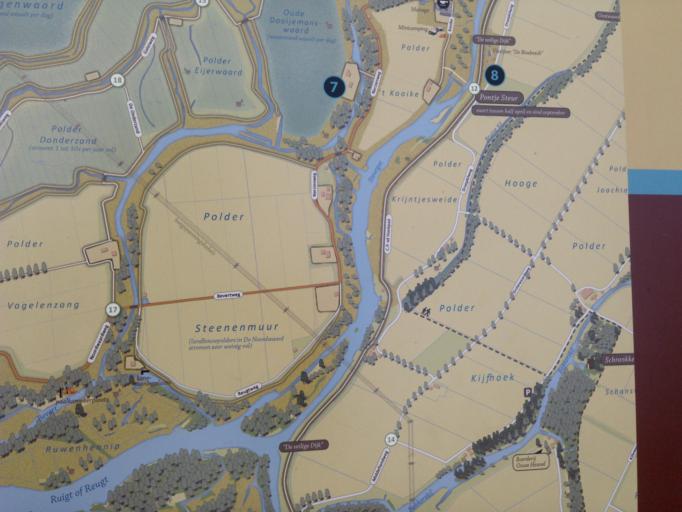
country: NL
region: North Brabant
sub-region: Gemeente Werkendam
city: Werkendam
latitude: 51.7939
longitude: 4.8712
